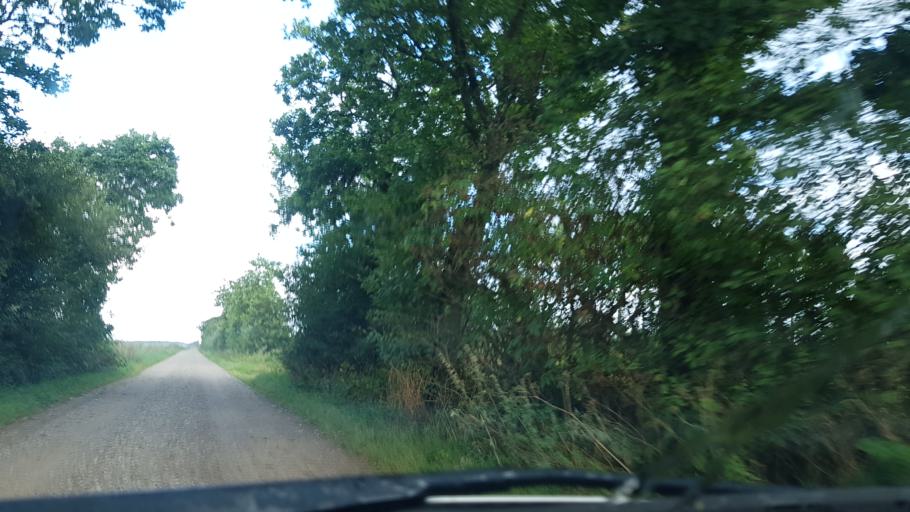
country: DK
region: South Denmark
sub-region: Tonder Kommune
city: Sherrebek
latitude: 55.2250
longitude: 8.7855
